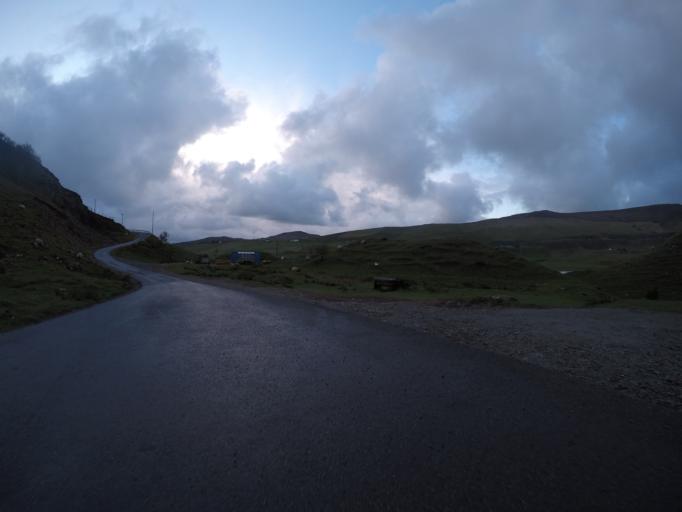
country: GB
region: Scotland
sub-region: Highland
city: Portree
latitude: 57.5847
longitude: -6.3330
